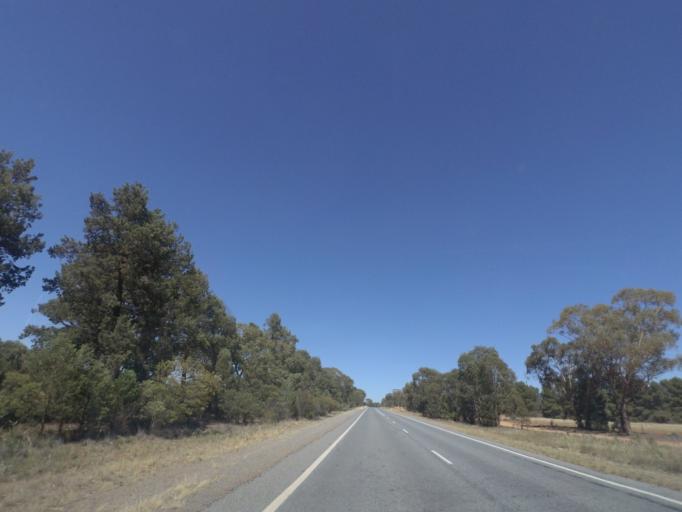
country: AU
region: New South Wales
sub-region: Narrandera
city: Narrandera
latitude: -34.4175
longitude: 146.8536
